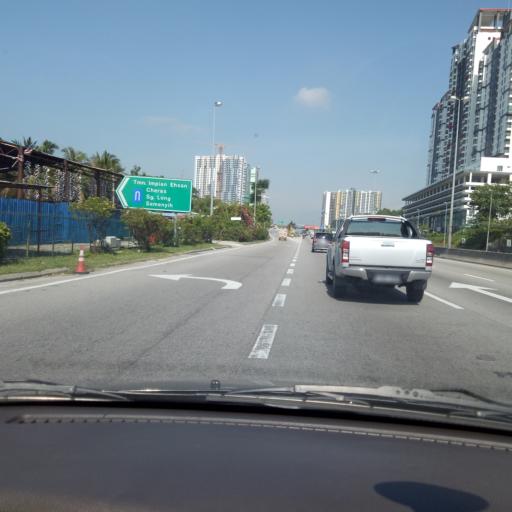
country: MY
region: Selangor
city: Kampong Baharu Balakong
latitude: 3.0297
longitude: 101.7607
